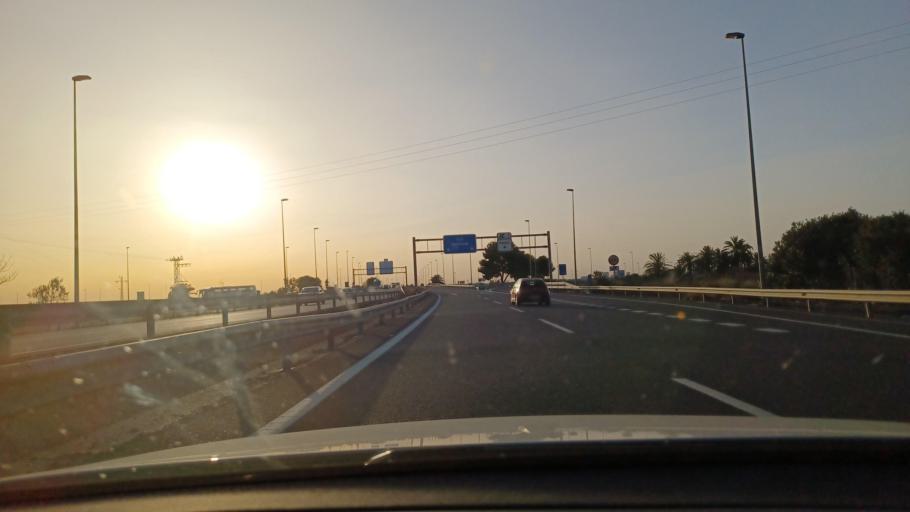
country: ES
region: Valencia
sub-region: Provincia de Valencia
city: Pucol
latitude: 39.6311
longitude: -0.3024
